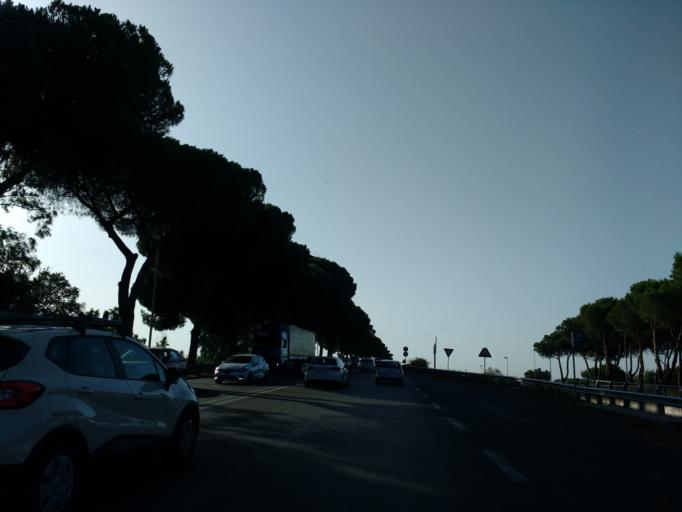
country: IT
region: Latium
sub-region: Citta metropolitana di Roma Capitale
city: Ciampino
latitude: 41.7756
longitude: 12.6082
